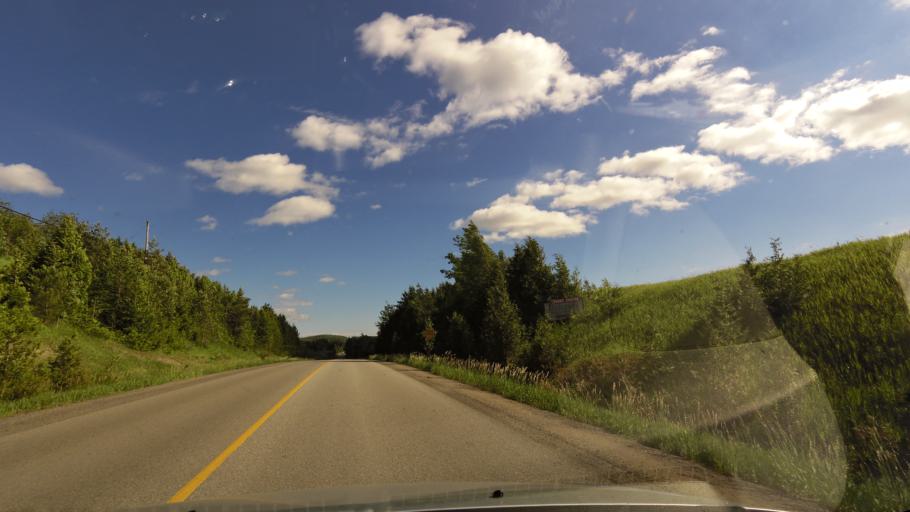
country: CA
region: Ontario
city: Bradford West Gwillimbury
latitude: 44.1933
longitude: -79.6234
